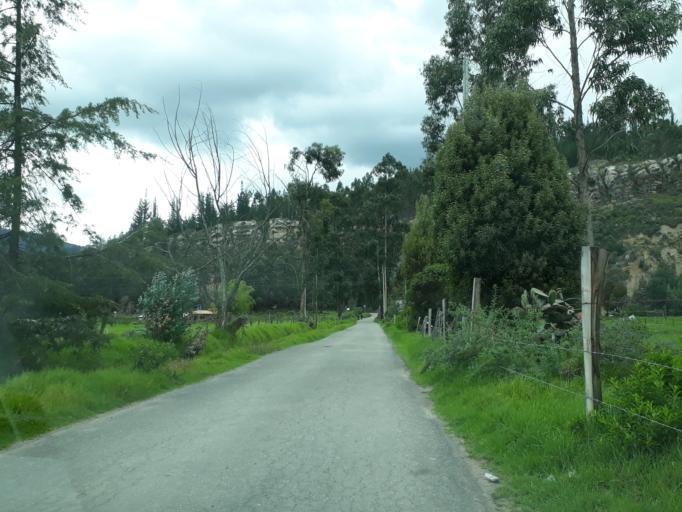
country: CO
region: Cundinamarca
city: Ubate
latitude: 5.2779
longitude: -73.8234
